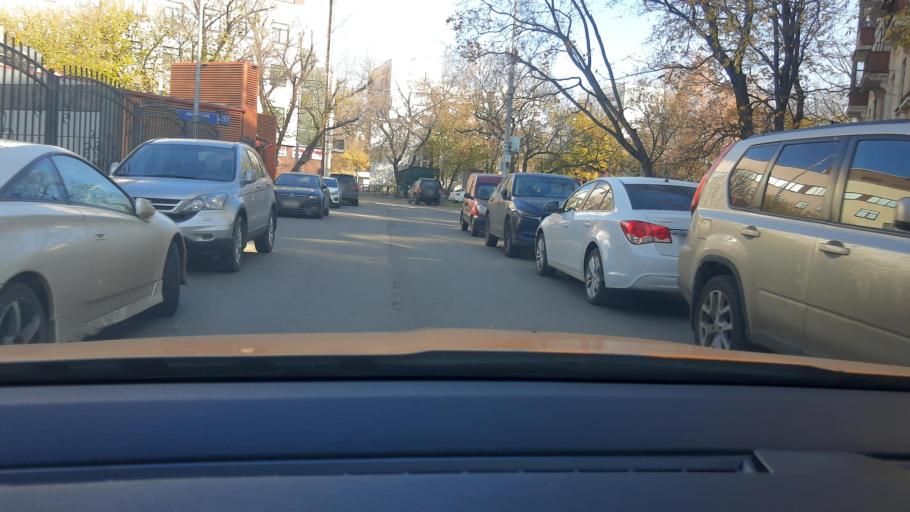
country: RU
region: Moscow
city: Novokuz'minki
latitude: 55.7171
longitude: 37.7853
